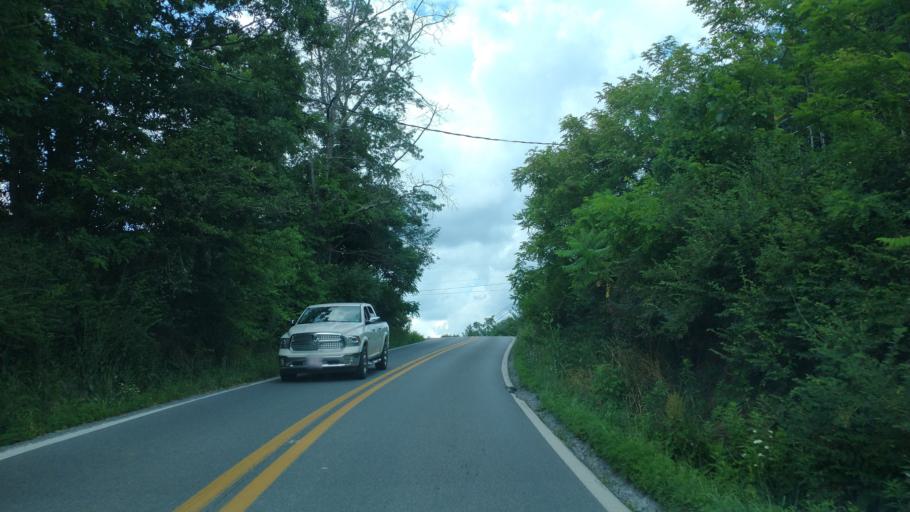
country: US
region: West Virginia
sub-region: Mercer County
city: Athens
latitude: 37.3943
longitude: -81.0590
